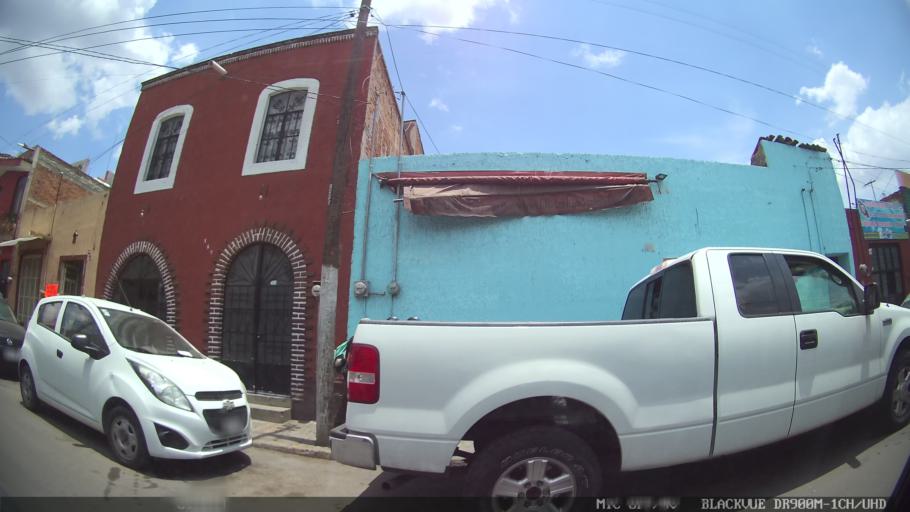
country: MX
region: Jalisco
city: Tonala
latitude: 20.6256
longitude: -103.2445
